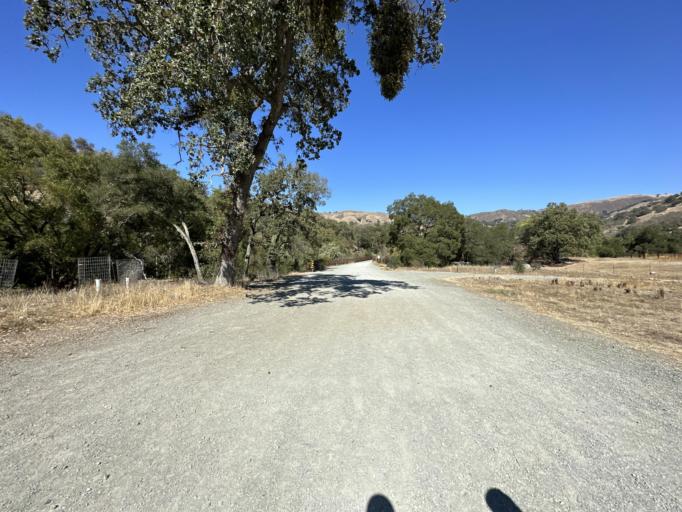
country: US
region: California
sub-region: Santa Clara County
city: Milpitas
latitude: 37.5079
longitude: -121.8287
